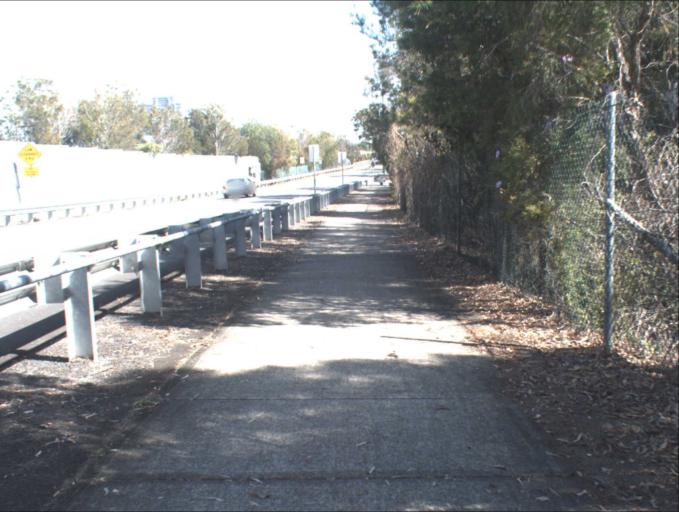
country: AU
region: Queensland
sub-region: Logan
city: Beenleigh
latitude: -27.6994
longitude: 153.1972
